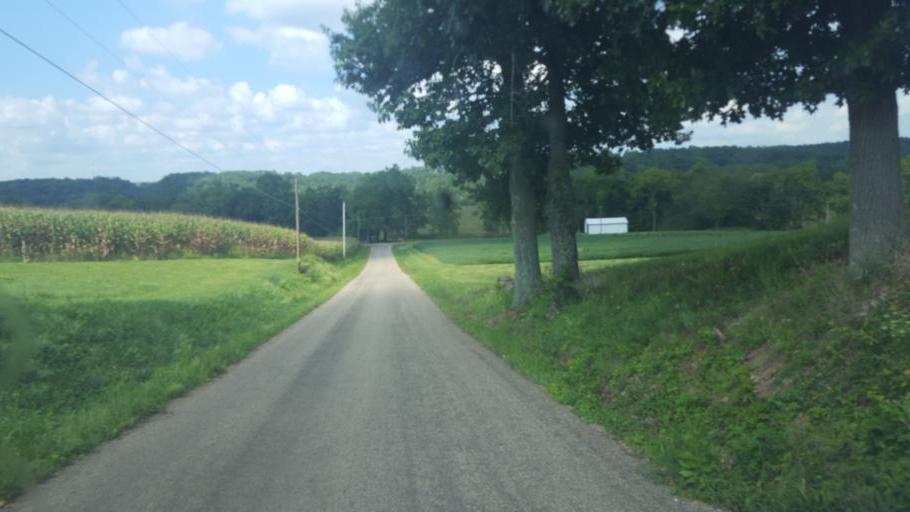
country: US
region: Ohio
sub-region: Knox County
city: Danville
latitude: 40.3984
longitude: -82.3101
